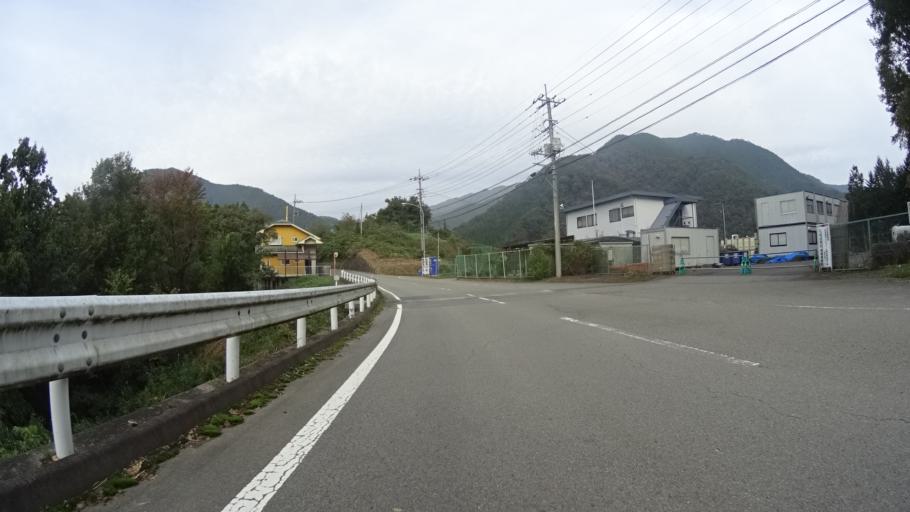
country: JP
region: Yamanashi
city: Uenohara
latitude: 35.6321
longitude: 139.0566
